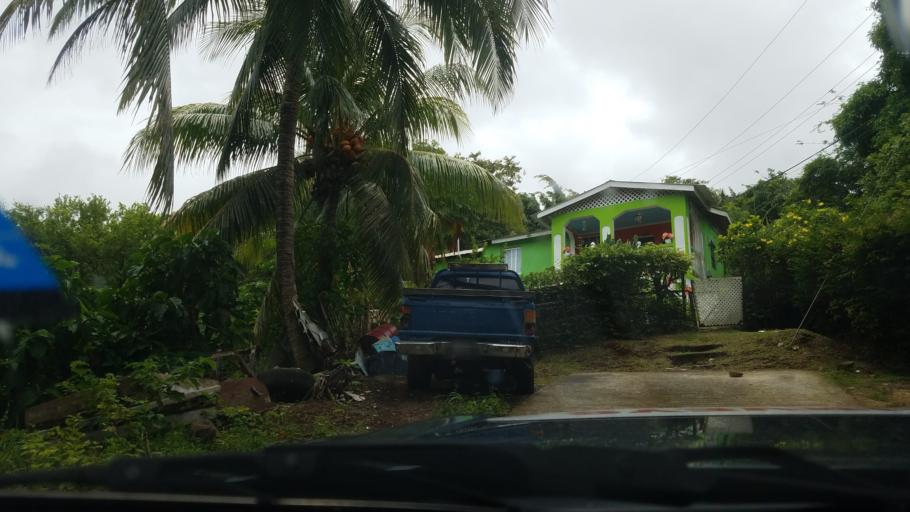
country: LC
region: Castries Quarter
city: Bisee
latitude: 14.0117
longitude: -60.9219
